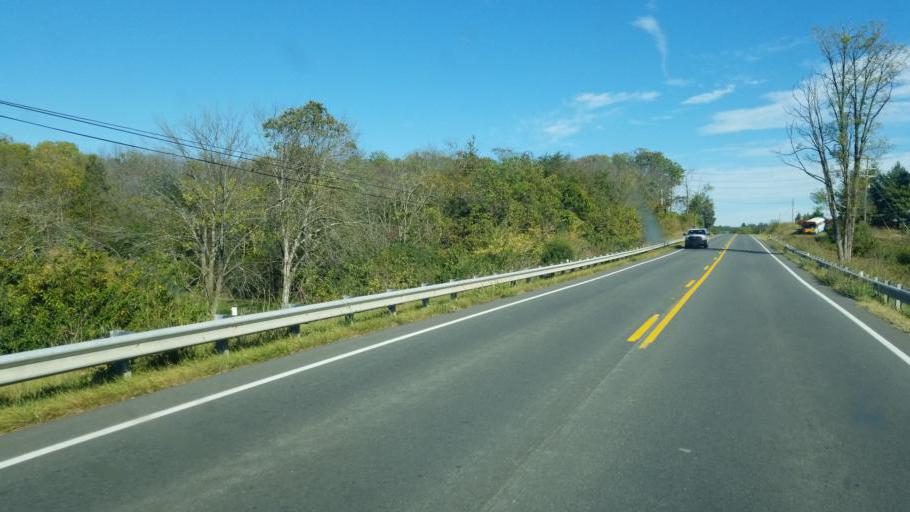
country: US
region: Virginia
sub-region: Warren County
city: Shenandoah Farms
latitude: 39.0582
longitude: -78.1158
